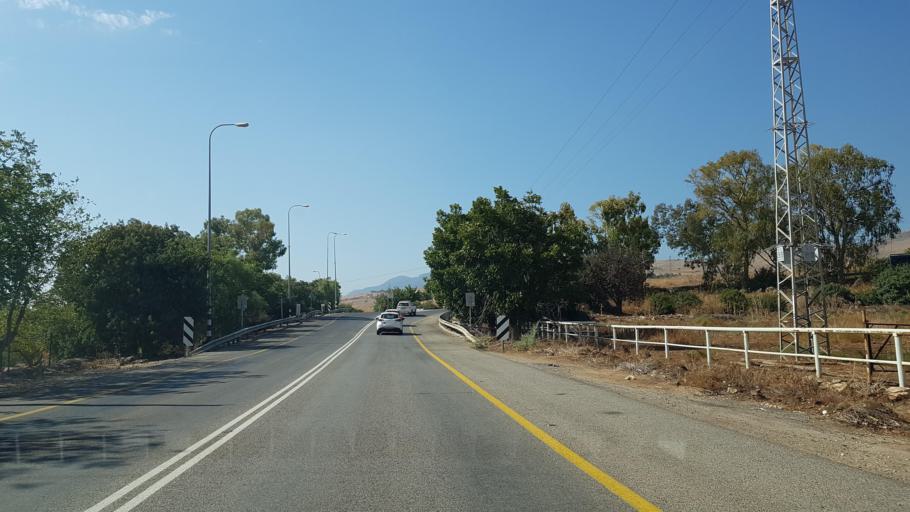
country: IL
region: Northern District
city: Rosh Pinna
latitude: 32.9043
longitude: 35.5493
